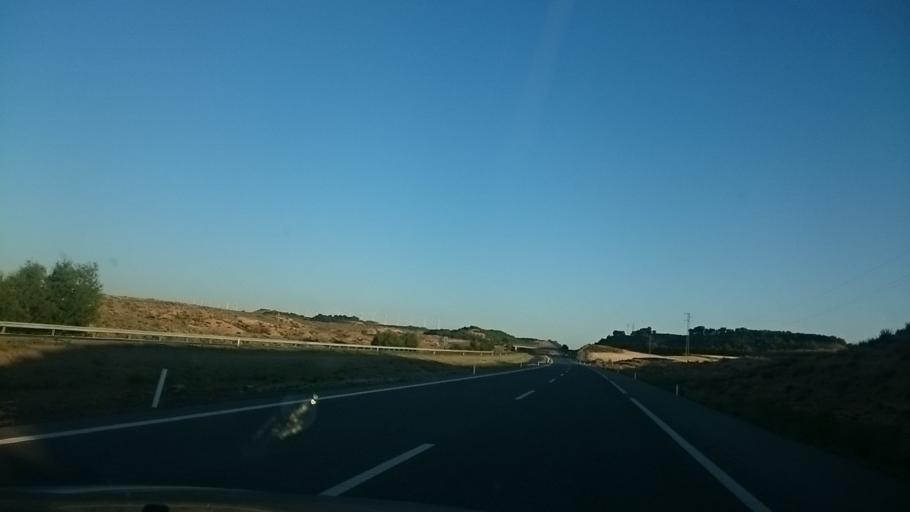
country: ES
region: Navarre
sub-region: Provincia de Navarra
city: Murchante
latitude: 42.0751
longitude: -1.6964
